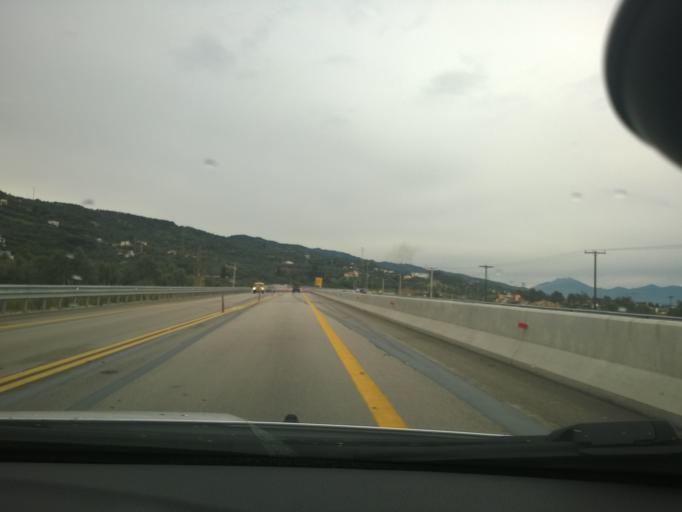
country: GR
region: West Greece
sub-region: Nomos Achaias
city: Selianitika
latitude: 38.2791
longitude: 22.0277
